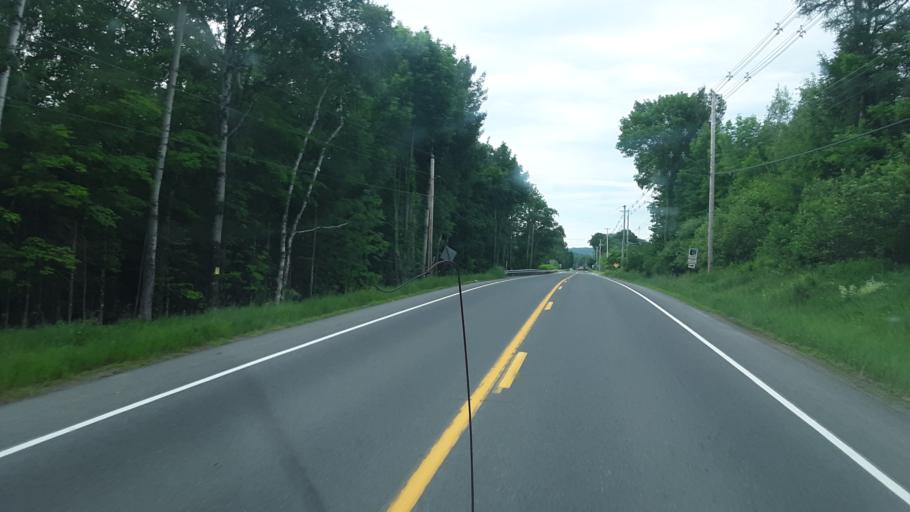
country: US
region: Maine
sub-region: Penobscot County
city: Patten
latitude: 45.8820
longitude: -68.4179
